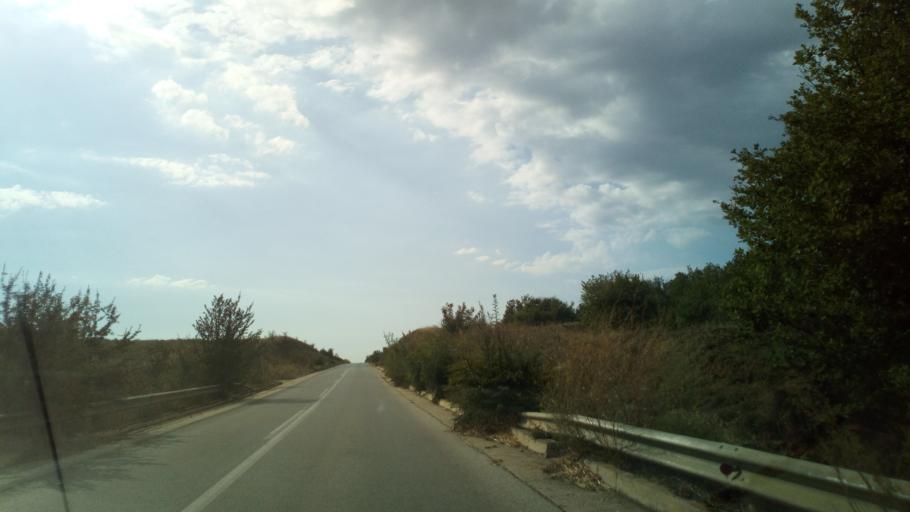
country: GR
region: Central Macedonia
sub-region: Nomos Thessalonikis
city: Gerakarou
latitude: 40.5926
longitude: 23.2381
